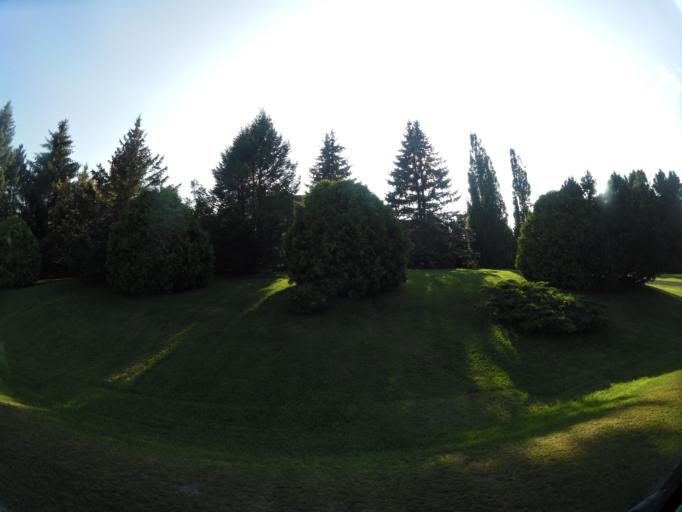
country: CA
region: Ontario
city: Clarence-Rockland
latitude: 45.4998
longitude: -75.4496
